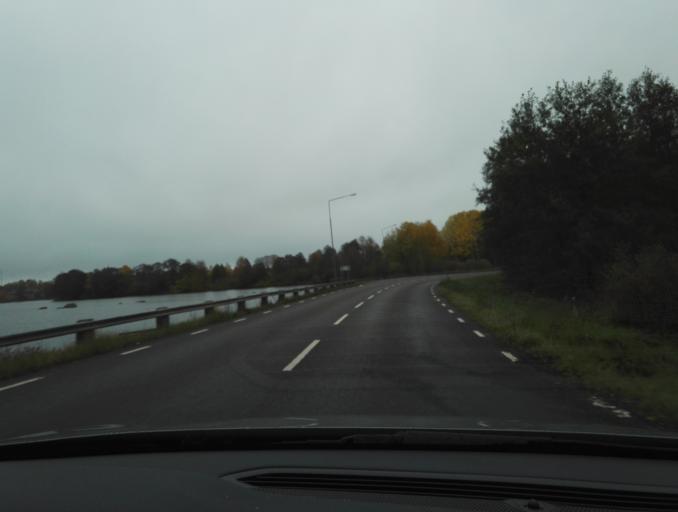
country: SE
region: Kronoberg
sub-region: Vaxjo Kommun
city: Rottne
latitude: 57.0259
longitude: 14.8761
